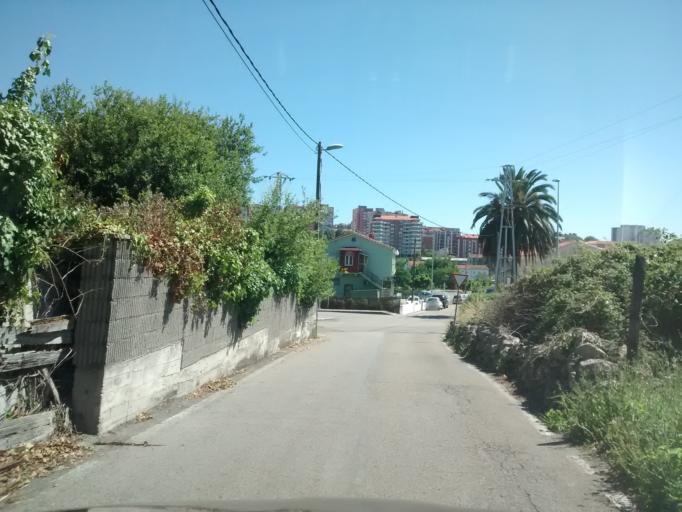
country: ES
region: Cantabria
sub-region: Provincia de Cantabria
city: Santander
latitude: 43.4685
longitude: -3.8300
